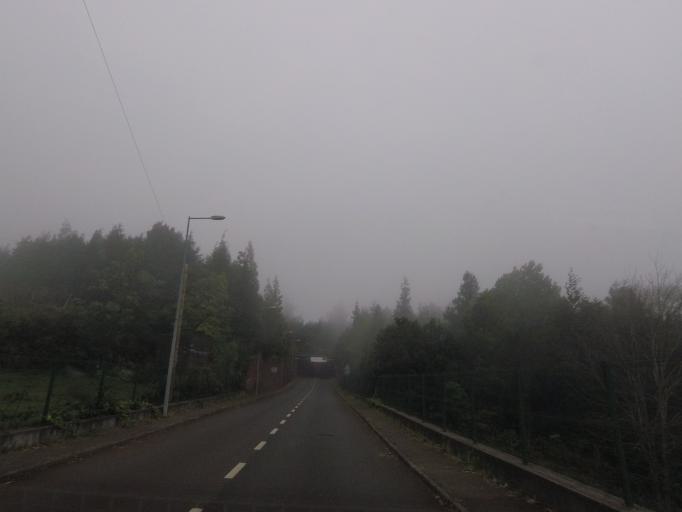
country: PT
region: Madeira
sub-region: Santa Cruz
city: Santa Cruz
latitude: 32.7238
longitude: -16.8245
